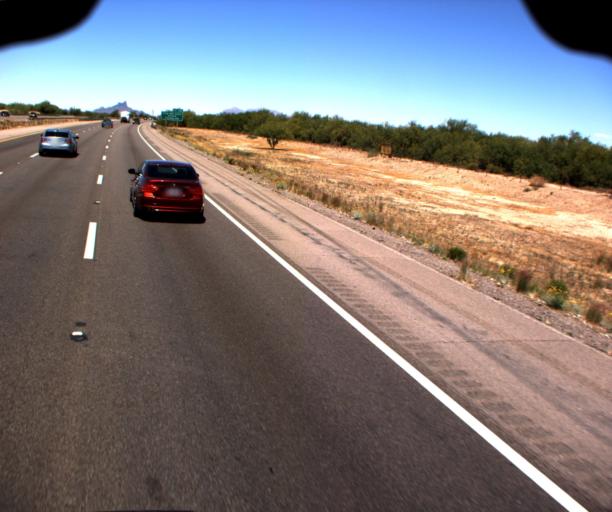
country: US
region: Arizona
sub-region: Pima County
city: Marana
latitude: 32.4945
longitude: -111.2613
